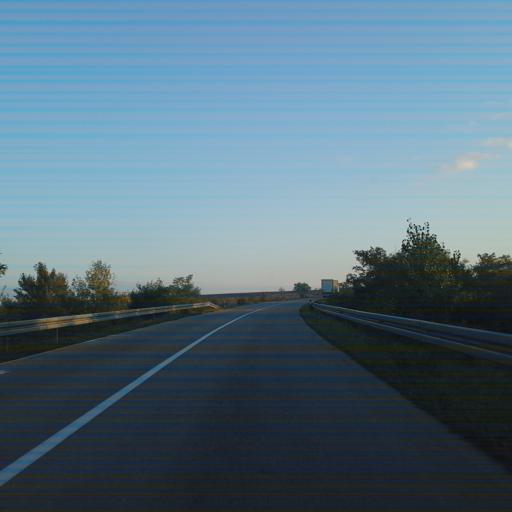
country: RS
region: Central Serbia
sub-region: Zajecarski Okrug
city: Zajecar
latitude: 44.0599
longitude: 22.3332
